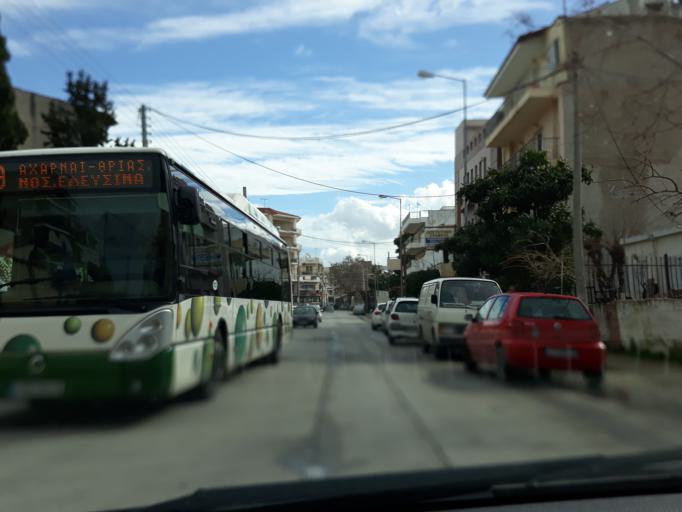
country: GR
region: Attica
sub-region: Nomarchia Anatolikis Attikis
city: Acharnes
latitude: 38.0830
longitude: 23.7310
